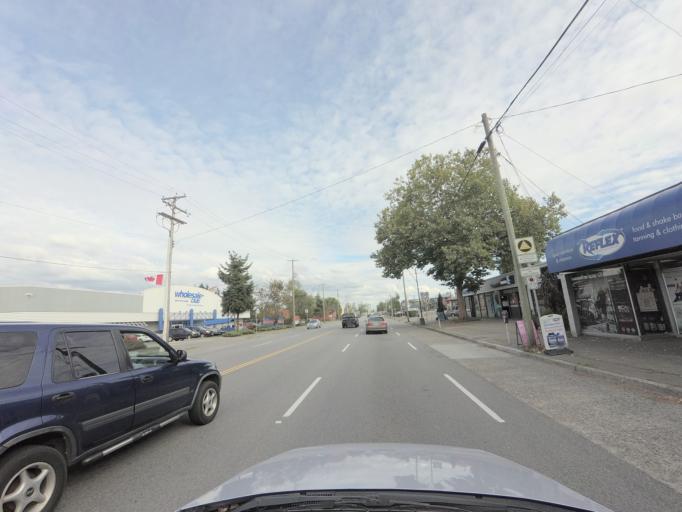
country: CA
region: British Columbia
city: Burnaby
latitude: 49.2243
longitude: -122.9869
